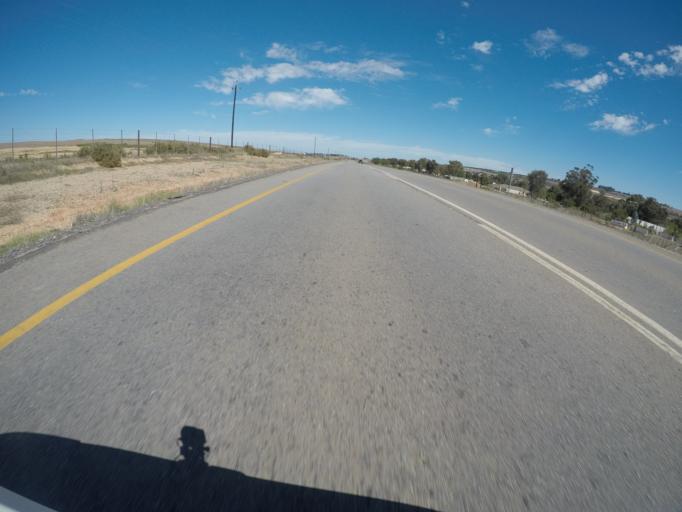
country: ZA
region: Western Cape
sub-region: West Coast District Municipality
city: Malmesbury
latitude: -33.4880
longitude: 18.6869
